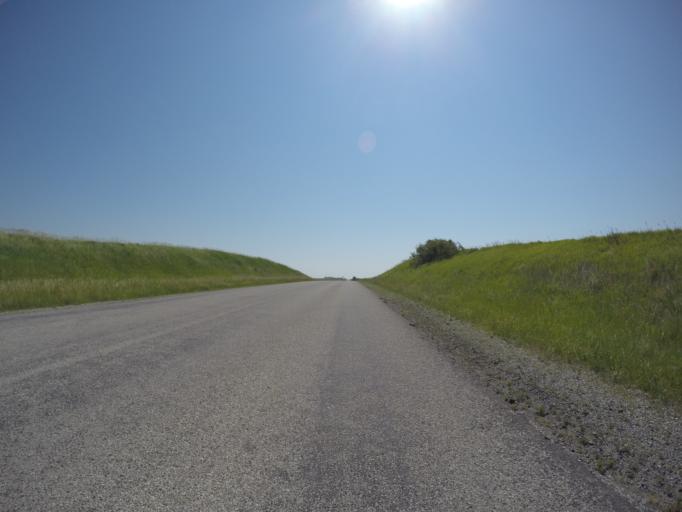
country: US
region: Kansas
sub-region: Doniphan County
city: Highland
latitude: 39.8565
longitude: -95.3761
